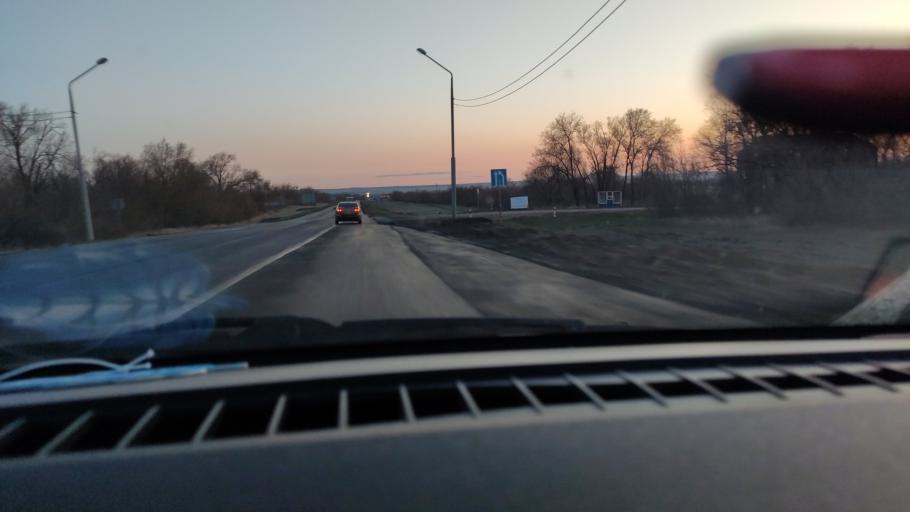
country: RU
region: Saratov
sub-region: Saratovskiy Rayon
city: Saratov
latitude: 51.6748
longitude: 46.0008
